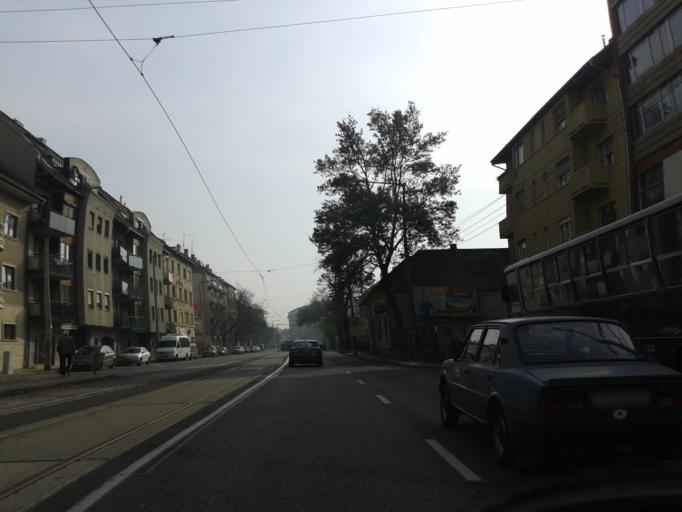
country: HU
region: Budapest
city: Budapest III. keruelet
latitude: 47.5357
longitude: 19.0336
